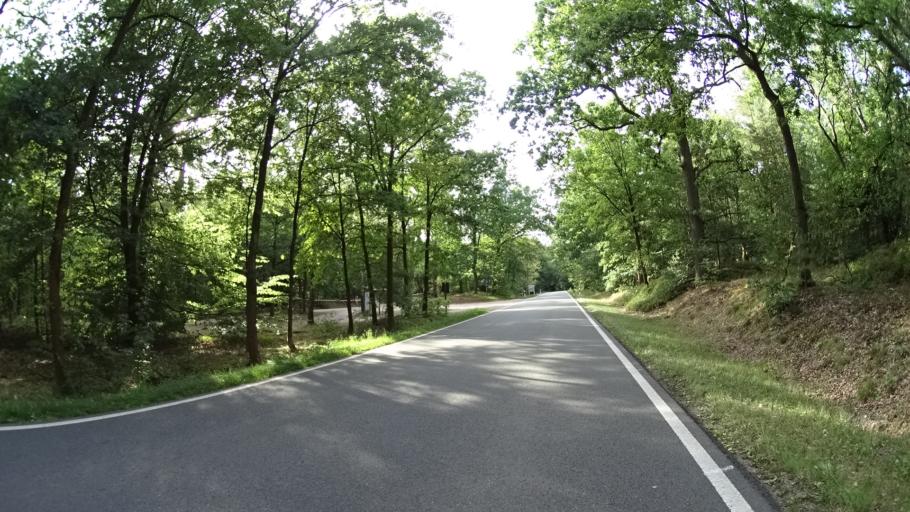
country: DE
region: Lower Saxony
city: Handeloh
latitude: 53.1749
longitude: 9.8879
